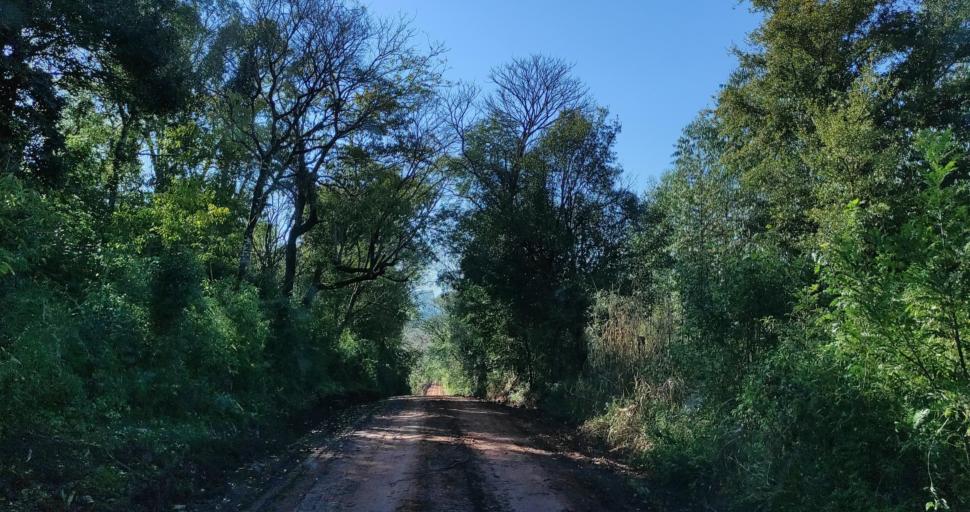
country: AR
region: Misiones
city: Capiovi
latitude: -26.8710
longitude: -55.0392
